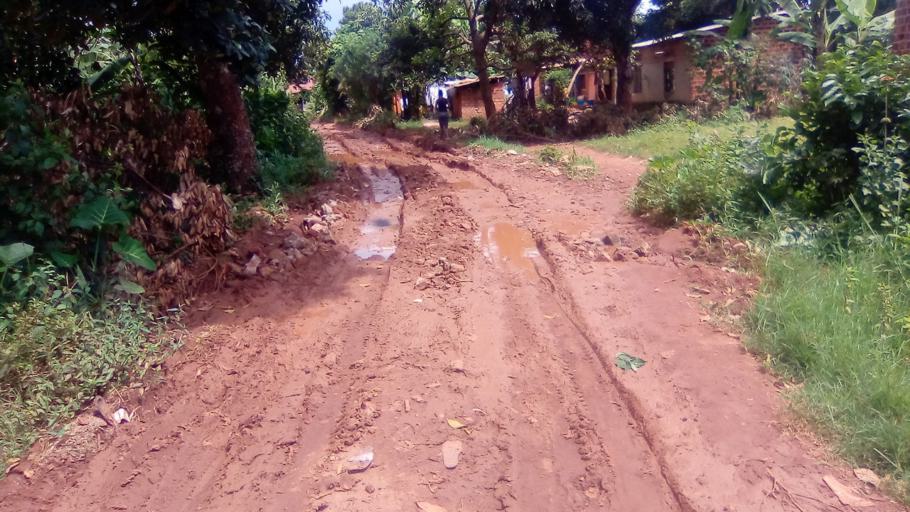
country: UG
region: Central Region
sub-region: Wakiso District
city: Entebbe
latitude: 0.1016
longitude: 32.5262
